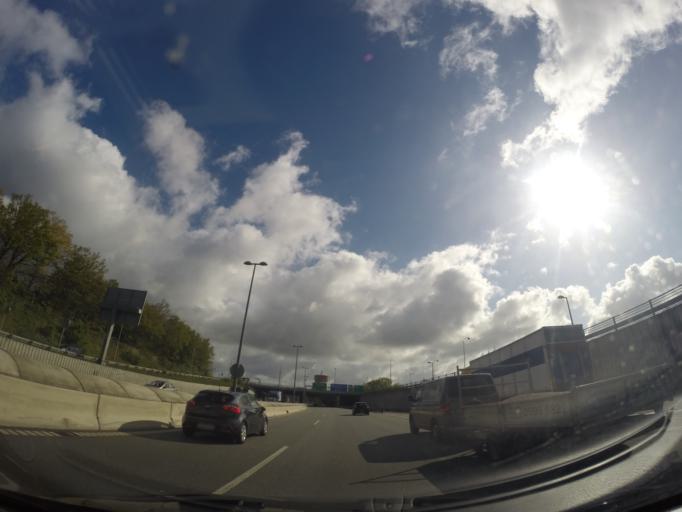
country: DK
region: Capital Region
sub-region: Gladsaxe Municipality
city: Buddinge
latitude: 55.7548
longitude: 12.4936
